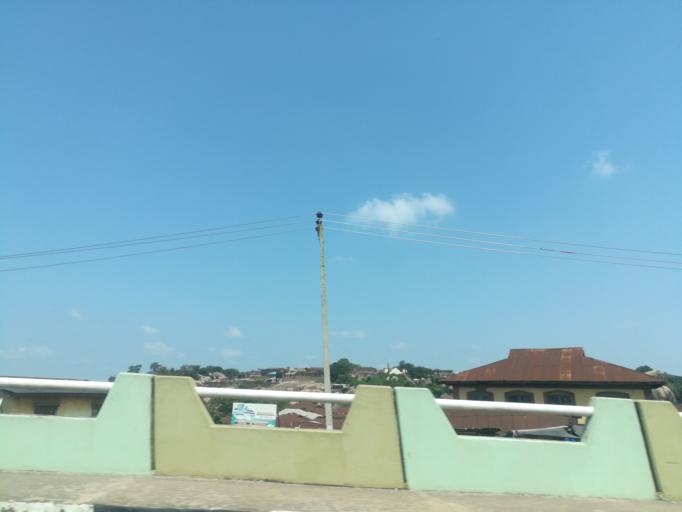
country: NG
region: Ogun
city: Abeokuta
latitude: 7.1567
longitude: 3.3430
